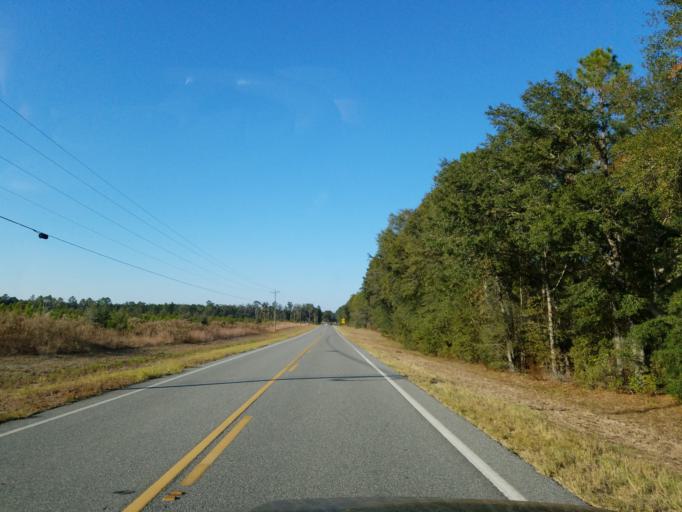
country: US
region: Georgia
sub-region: Echols County
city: Statenville
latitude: 30.6892
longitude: -83.0619
